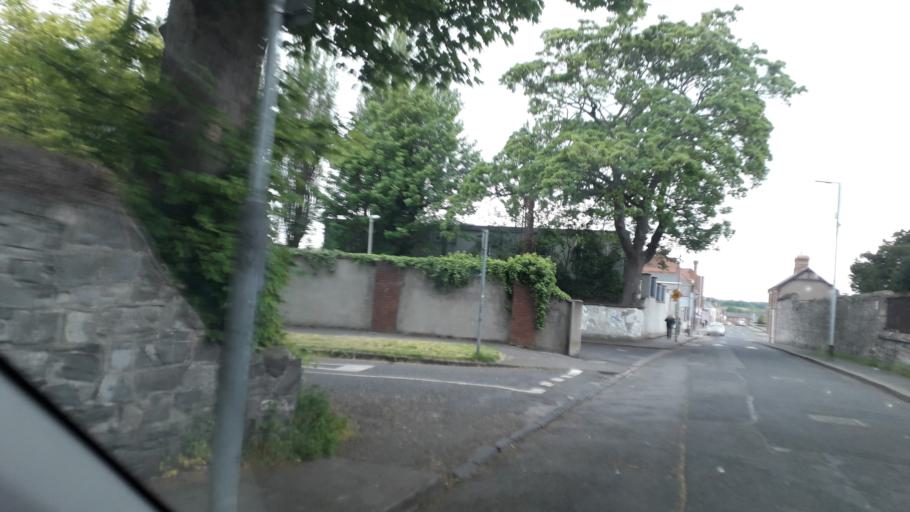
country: IE
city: Greenhills
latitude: 53.3360
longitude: -6.3178
